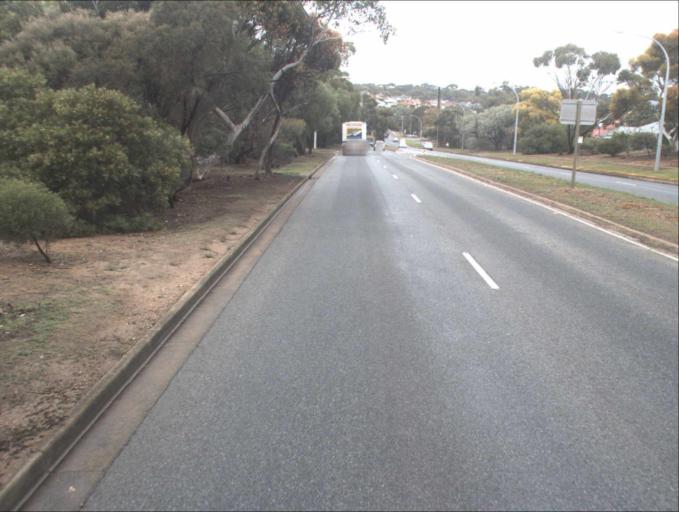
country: AU
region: South Australia
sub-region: Salisbury
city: Ingle Farm
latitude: -34.8373
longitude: 138.6456
